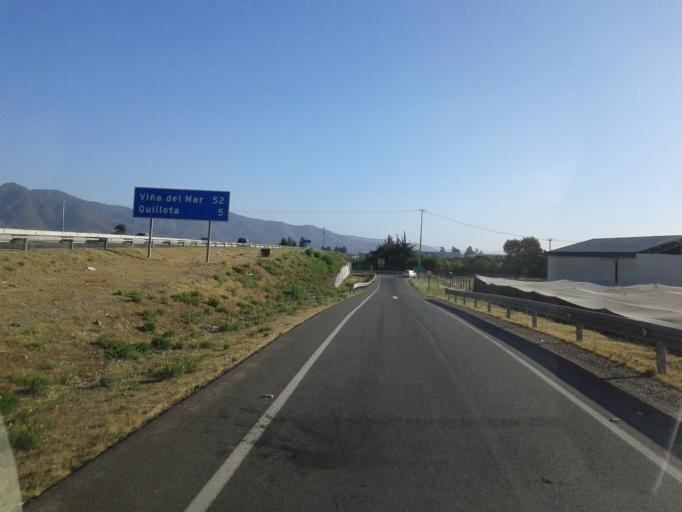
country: CL
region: Valparaiso
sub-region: Provincia de Quillota
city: Quillota
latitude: -32.8574
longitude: -71.2249
